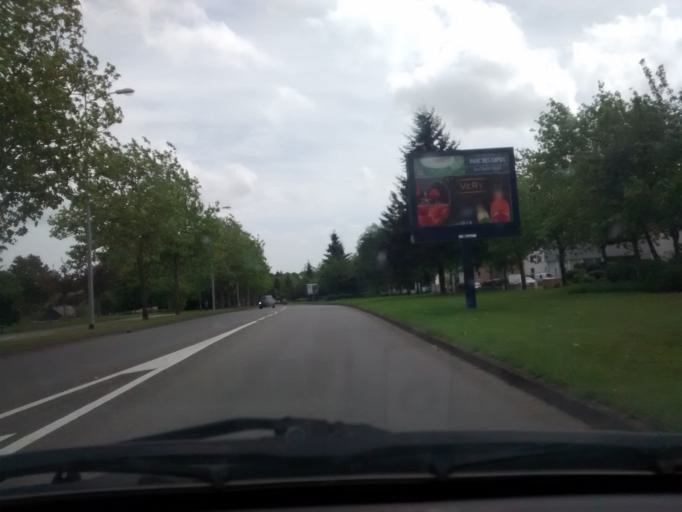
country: FR
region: Brittany
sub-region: Departement du Morbihan
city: Vannes
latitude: 47.6505
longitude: -2.7831
